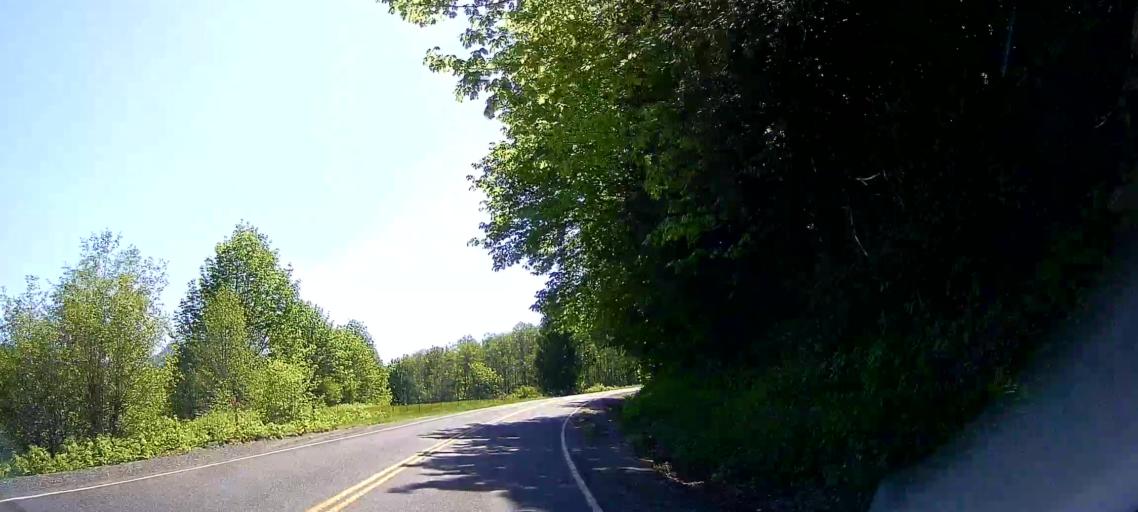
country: US
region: Washington
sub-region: Snohomish County
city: Darrington
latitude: 48.4687
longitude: -121.6184
